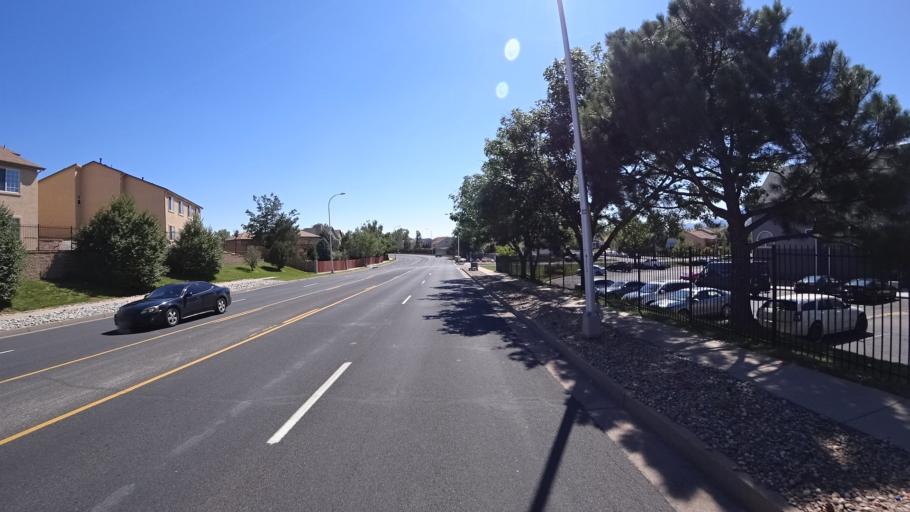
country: US
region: Colorado
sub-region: El Paso County
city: Stratmoor
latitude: 38.8224
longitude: -104.7506
